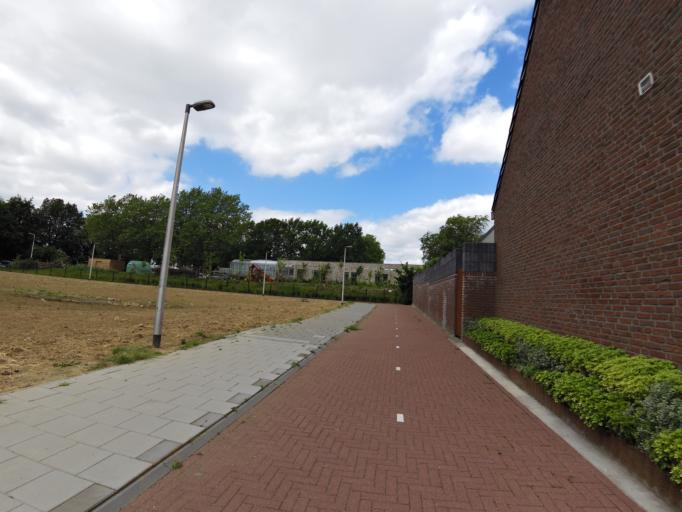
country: NL
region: Limburg
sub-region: Gemeente Kerkrade
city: Kerkrade
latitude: 50.8566
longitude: 6.0215
